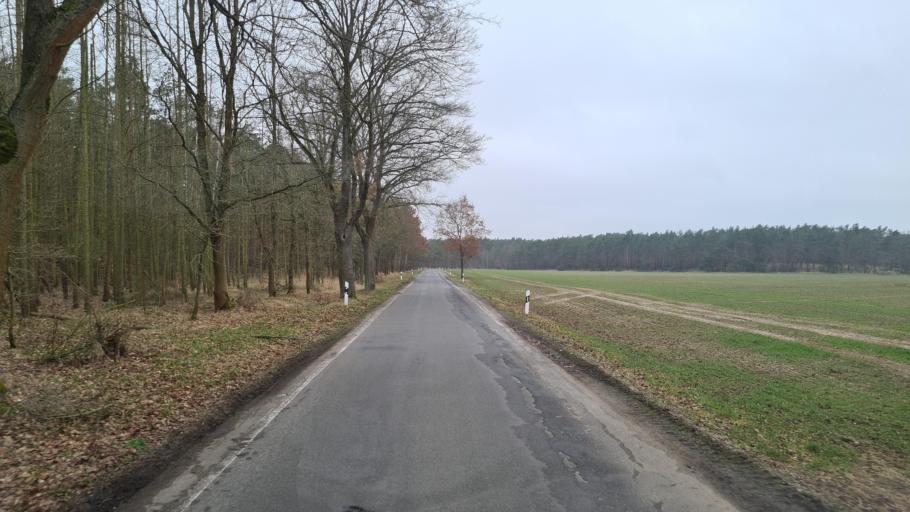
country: DE
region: Brandenburg
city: Herzberg
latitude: 51.6887
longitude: 13.1918
